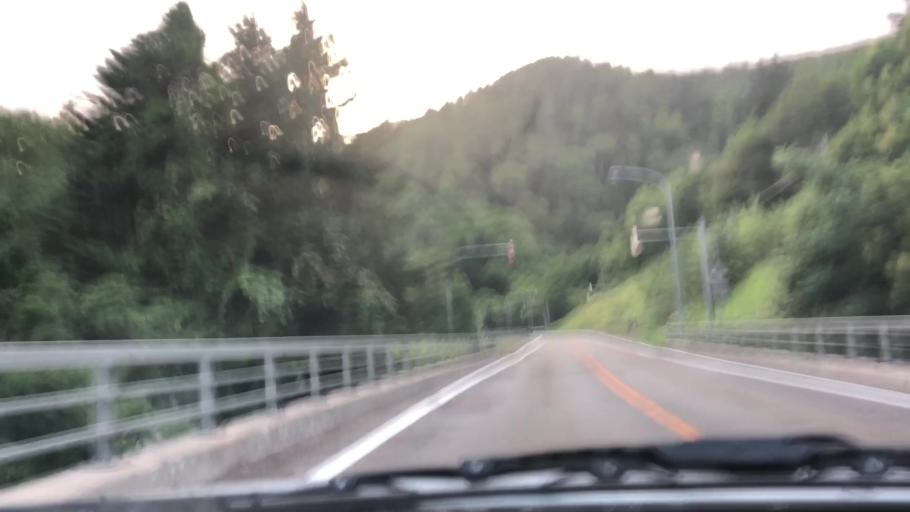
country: JP
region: Hokkaido
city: Shimo-furano
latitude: 42.9088
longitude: 142.3551
